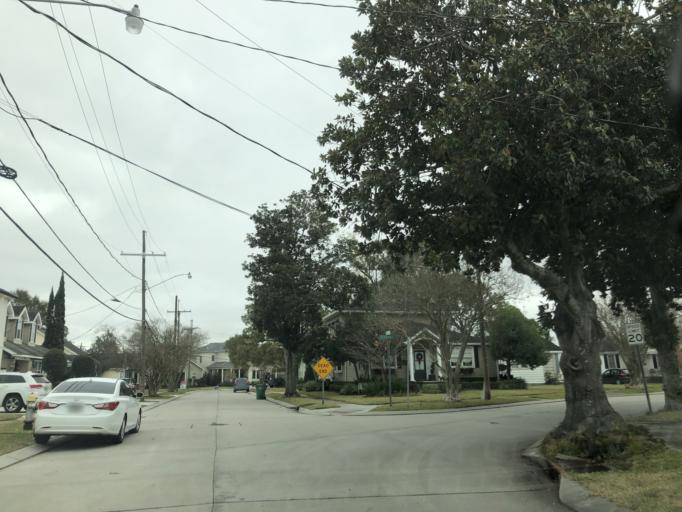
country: US
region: Louisiana
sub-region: Jefferson Parish
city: Metairie
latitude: 29.9770
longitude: -90.1539
